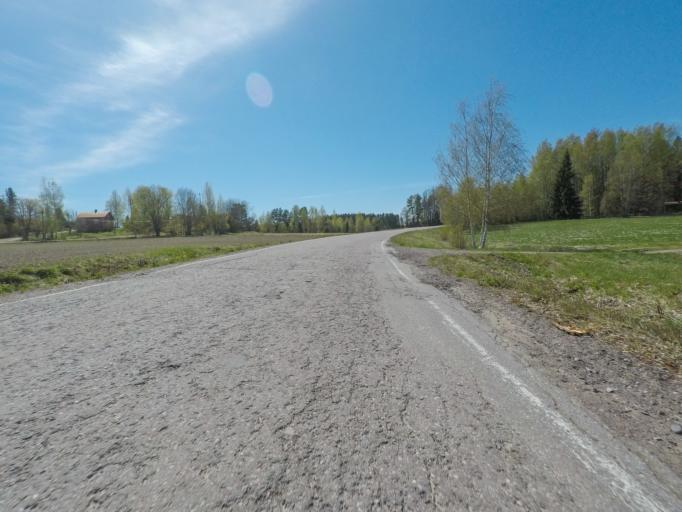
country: FI
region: Uusimaa
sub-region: Helsinki
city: Kaerkoelae
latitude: 60.5828
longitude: 23.7932
